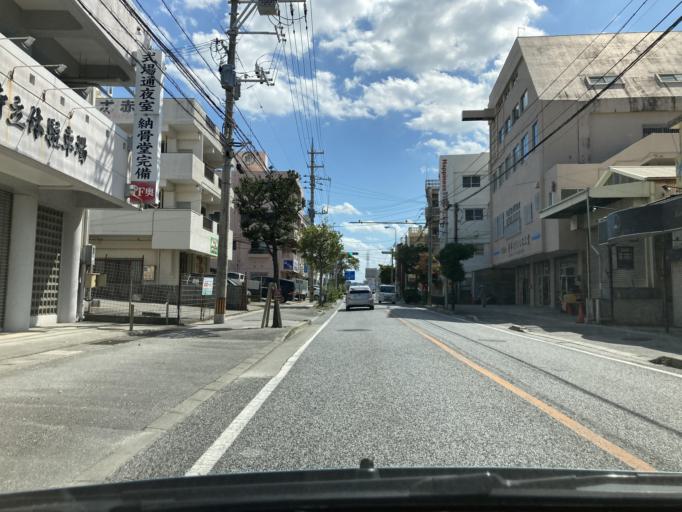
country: JP
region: Okinawa
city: Tomigusuku
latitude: 26.1943
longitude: 127.7060
